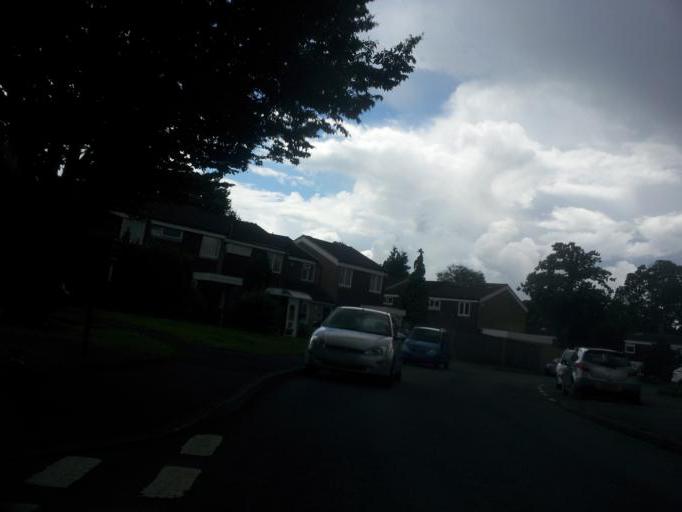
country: GB
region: England
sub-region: Kent
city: Meopham
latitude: 51.3318
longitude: 0.3659
